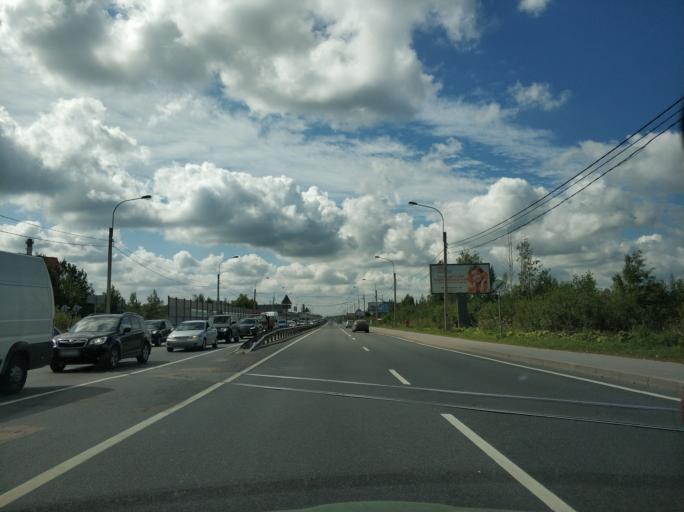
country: RU
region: Leningrad
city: Vsevolozhsk
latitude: 60.0306
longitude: 30.6250
